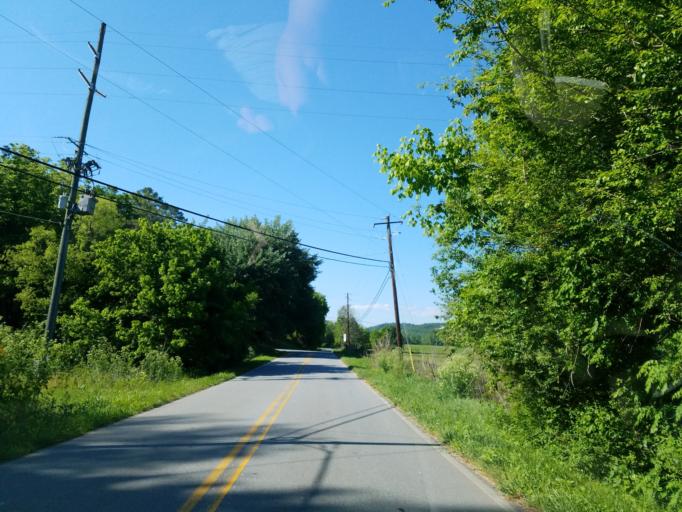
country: US
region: Georgia
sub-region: Pickens County
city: Jasper
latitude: 34.5648
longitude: -84.5115
